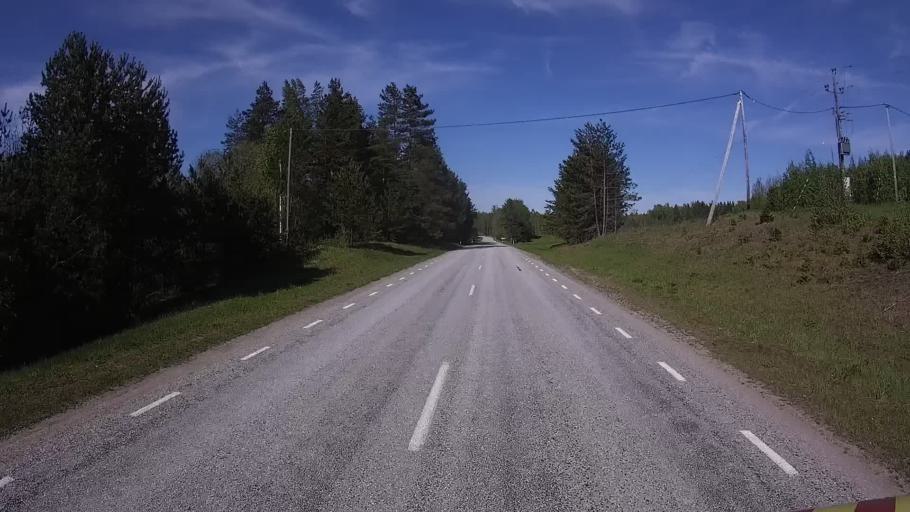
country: EE
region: Vorumaa
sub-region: Antsla vald
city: Vana-Antsla
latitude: 57.9905
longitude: 26.4872
